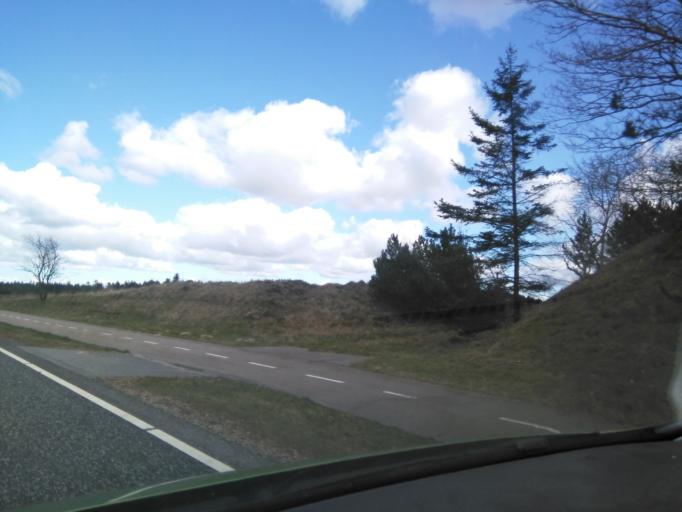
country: DK
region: Central Jutland
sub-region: Ikast-Brande Kommune
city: Bording Kirkeby
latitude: 56.1456
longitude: 9.3526
